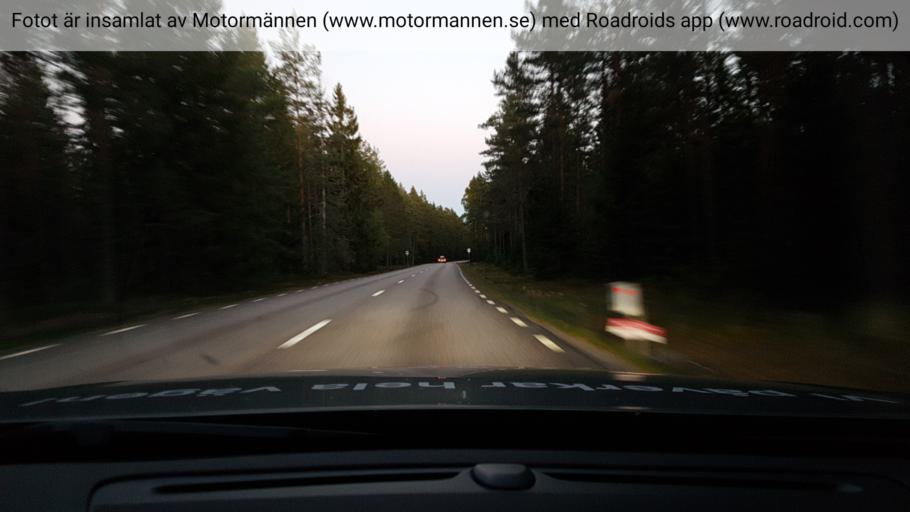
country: SE
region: OErebro
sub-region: Askersunds Kommun
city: Askersund
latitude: 58.8774
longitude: 14.7693
